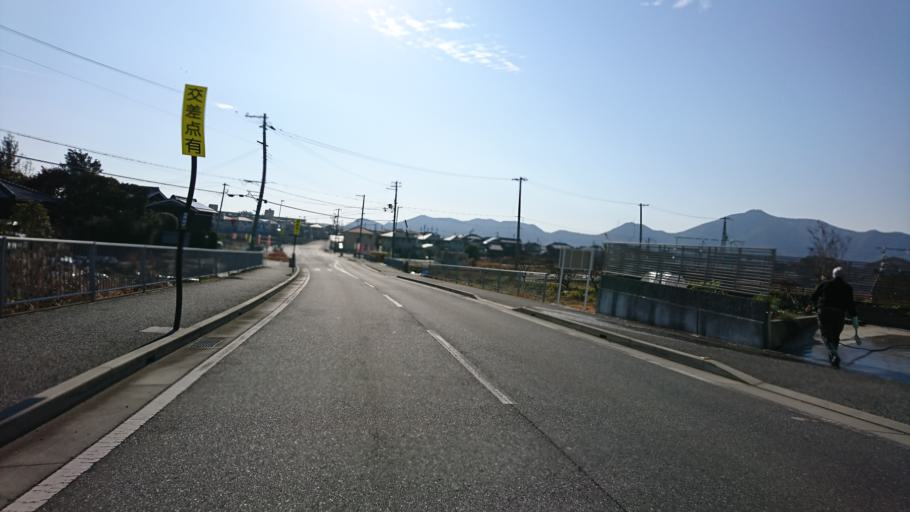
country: JP
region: Hyogo
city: Kakogawacho-honmachi
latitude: 34.8229
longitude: 134.8246
